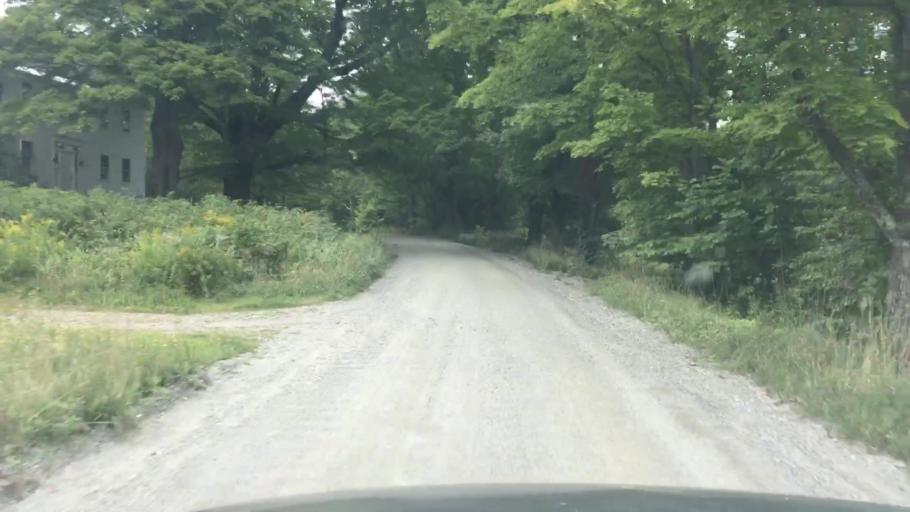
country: US
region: Vermont
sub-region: Windham County
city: Dover
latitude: 42.8506
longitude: -72.7756
